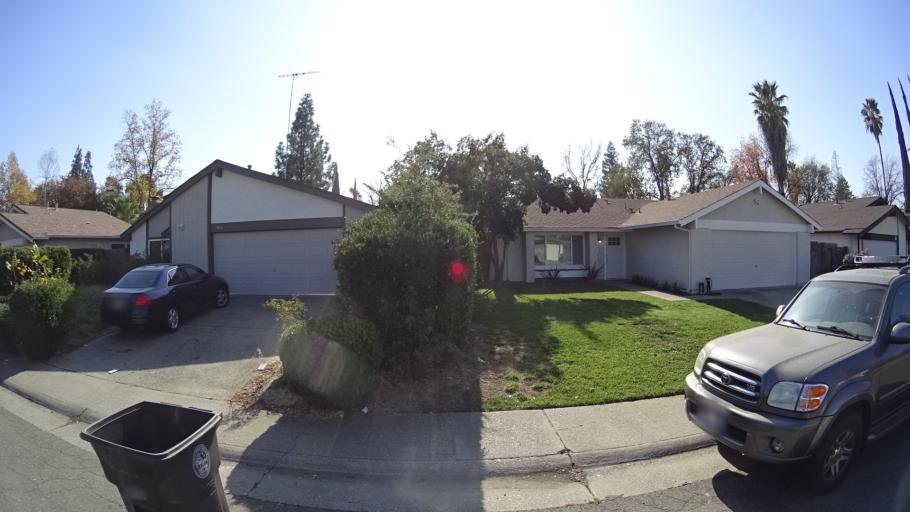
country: US
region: California
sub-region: Sacramento County
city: Citrus Heights
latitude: 38.6898
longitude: -121.2635
